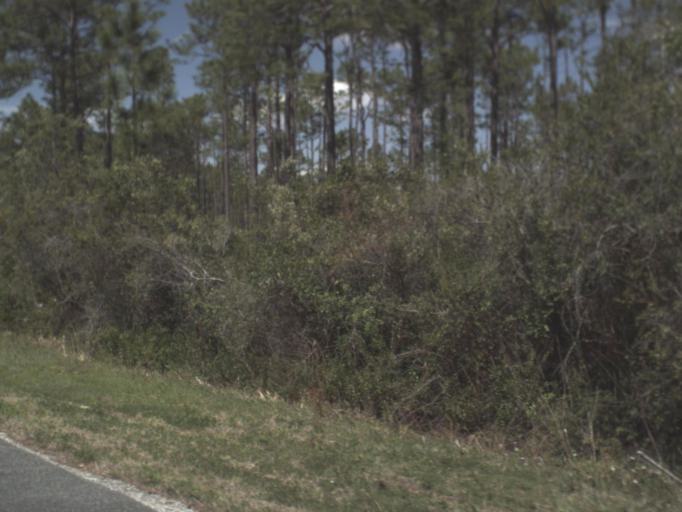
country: US
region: Florida
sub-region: Gadsden County
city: Midway
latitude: 30.3458
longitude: -84.5027
